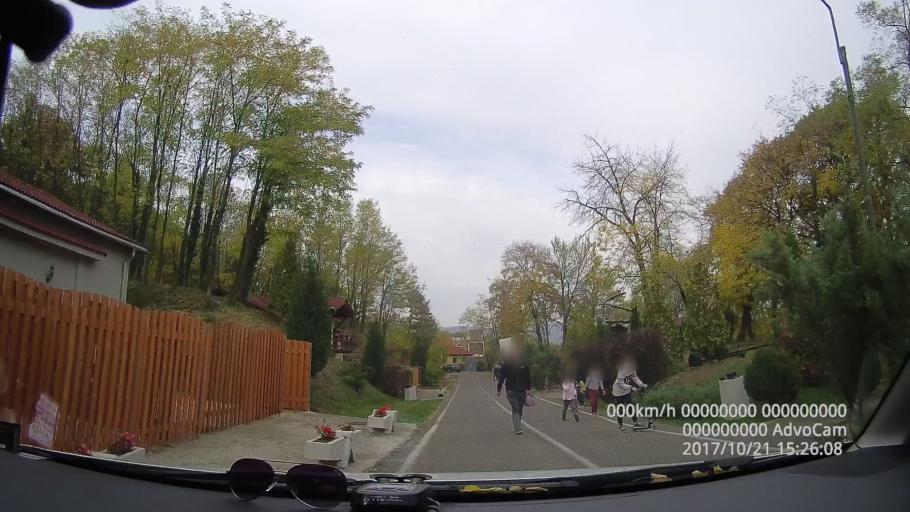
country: RO
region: Hunedoara
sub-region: Municipiul Deva
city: Deva
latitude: 45.8661
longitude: 22.9233
